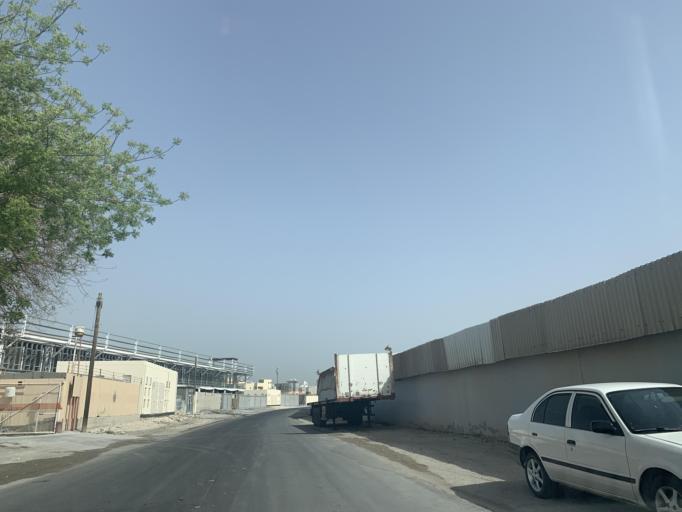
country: BH
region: Northern
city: Sitrah
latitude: 26.1537
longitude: 50.6178
